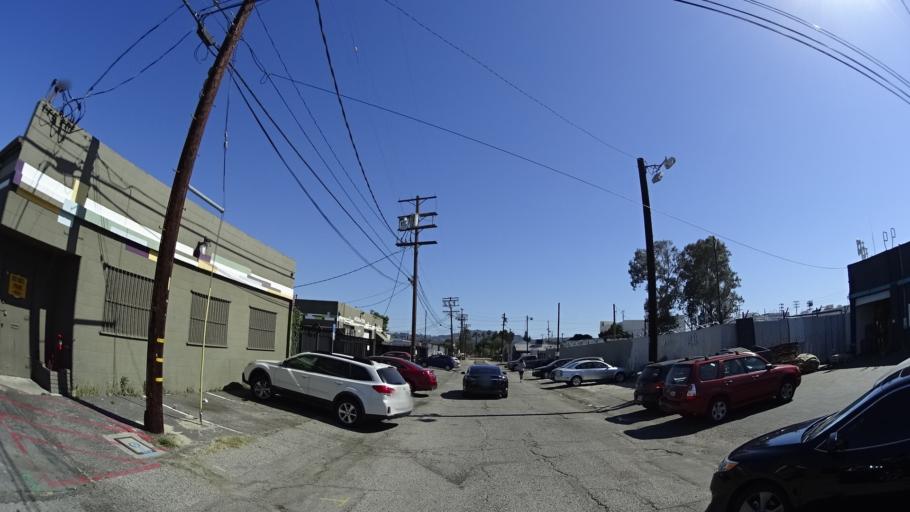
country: US
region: California
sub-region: Los Angeles County
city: North Hollywood
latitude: 34.1703
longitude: -118.3686
